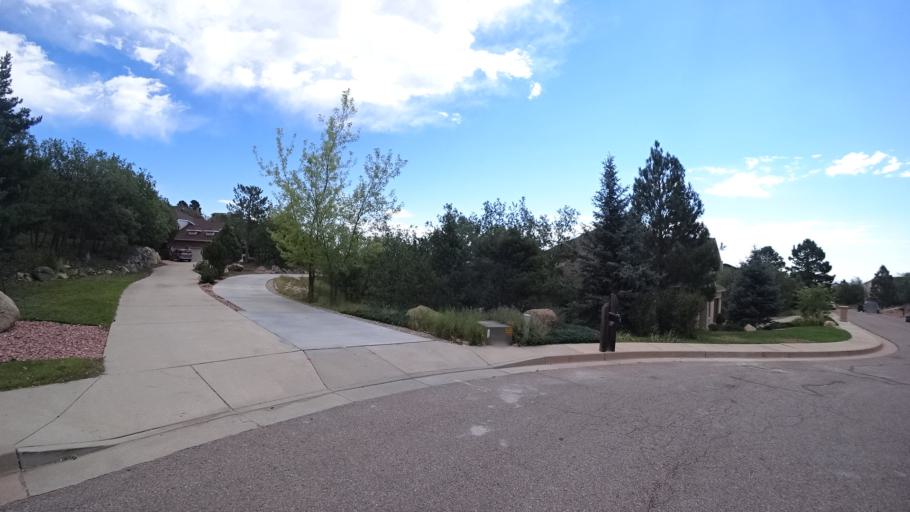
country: US
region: Colorado
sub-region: El Paso County
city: Fort Carson
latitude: 38.7639
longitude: -104.8245
